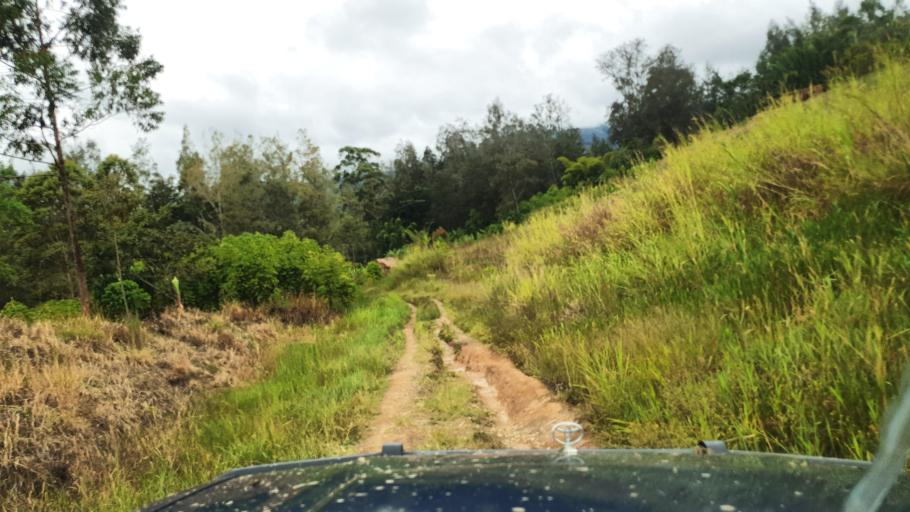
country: PG
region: Jiwaka
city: Minj
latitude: -5.9288
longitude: 144.7481
